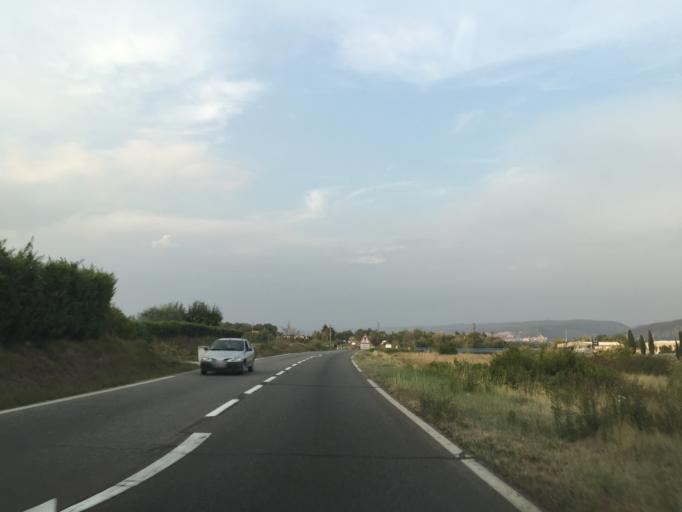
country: FR
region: Provence-Alpes-Cote d'Azur
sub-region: Departement des Alpes-de-Haute-Provence
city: Villeneuve
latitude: 43.8920
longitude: 5.8731
